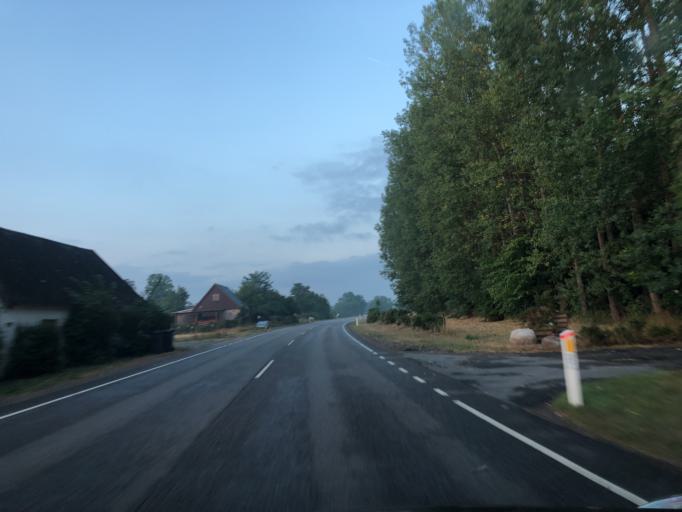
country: DK
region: Zealand
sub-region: Soro Kommune
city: Stenlille
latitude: 55.5695
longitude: 11.6435
